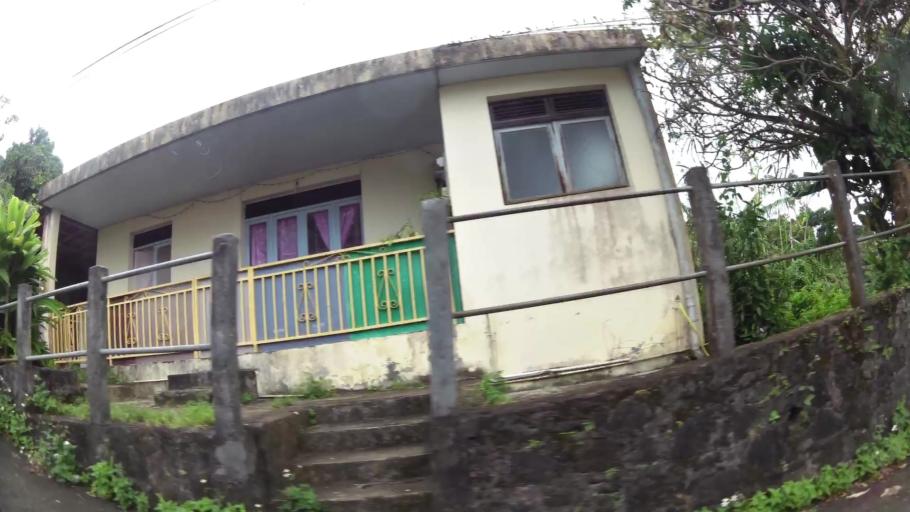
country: GP
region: Guadeloupe
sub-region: Guadeloupe
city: Trois-Rivieres
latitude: 15.9931
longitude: -61.6550
